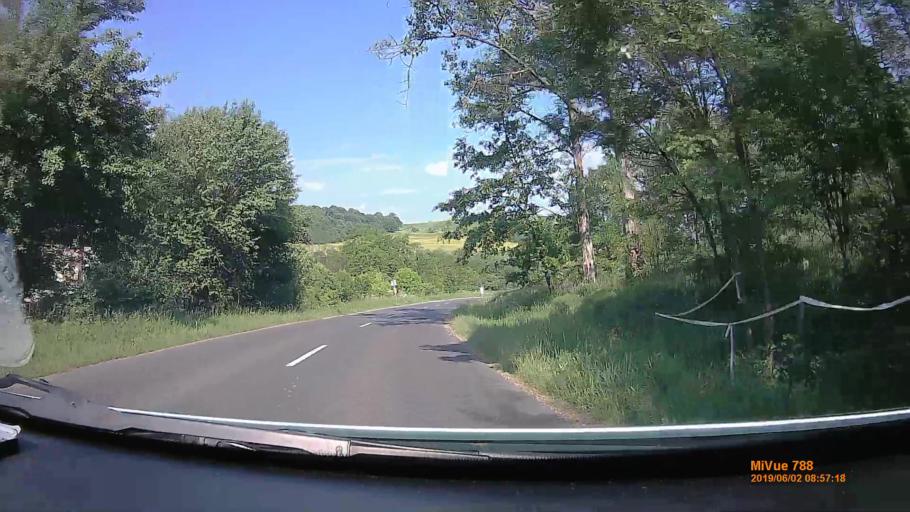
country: HU
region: Borsod-Abauj-Zemplen
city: Sajobabony
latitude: 48.1554
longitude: 20.6414
